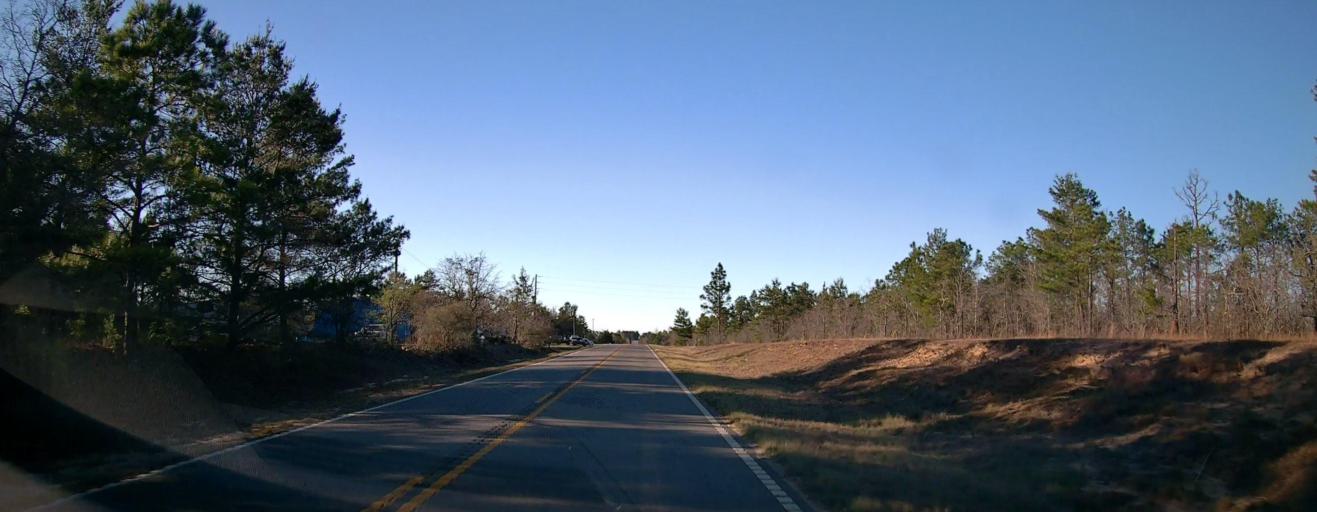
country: US
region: Georgia
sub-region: Talbot County
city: Talbotton
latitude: 32.5802
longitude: -84.4457
